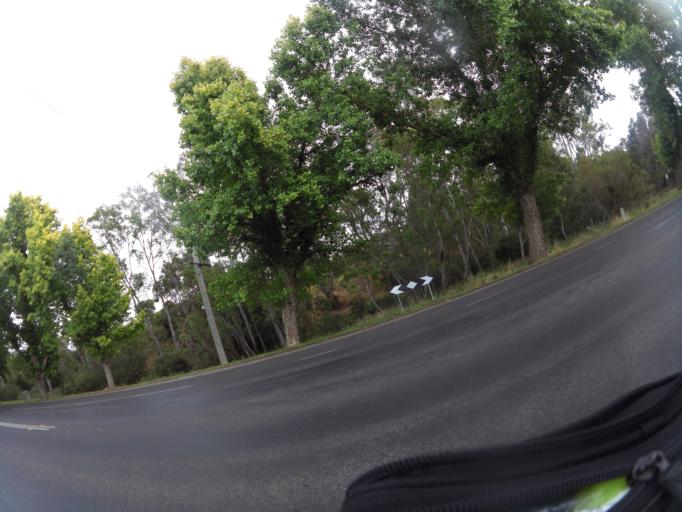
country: AU
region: Victoria
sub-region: Mount Alexander
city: Castlemaine
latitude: -37.0713
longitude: 144.2103
